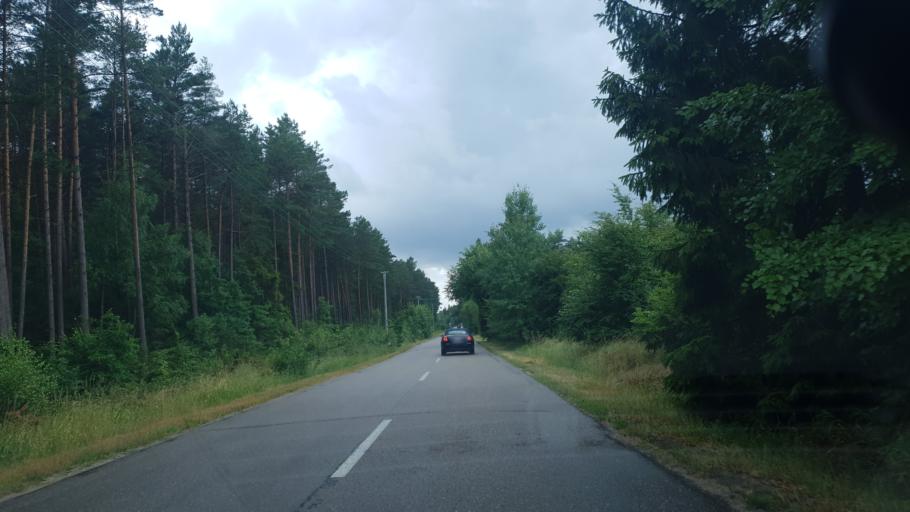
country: PL
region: Pomeranian Voivodeship
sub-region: Powiat kartuski
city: Stezyca
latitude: 54.2500
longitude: 18.0069
